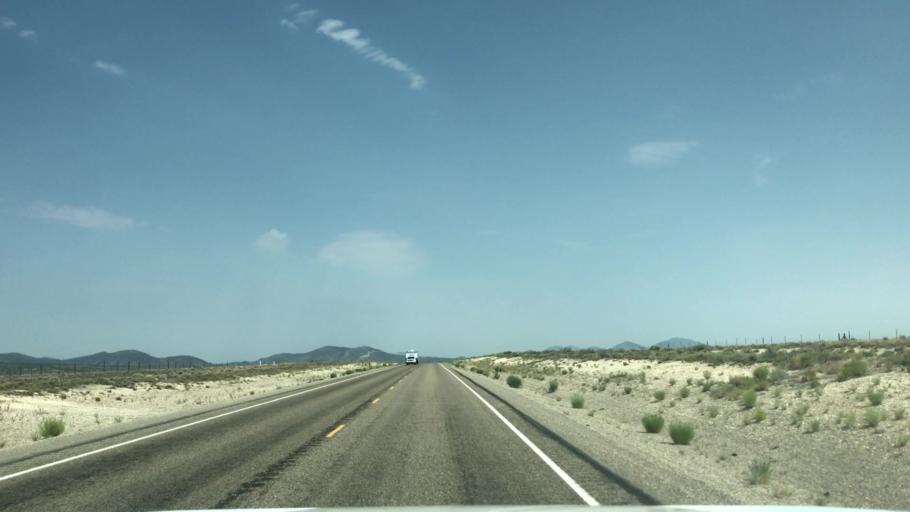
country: US
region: Nevada
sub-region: White Pine County
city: Ely
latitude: 39.1518
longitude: -114.7968
